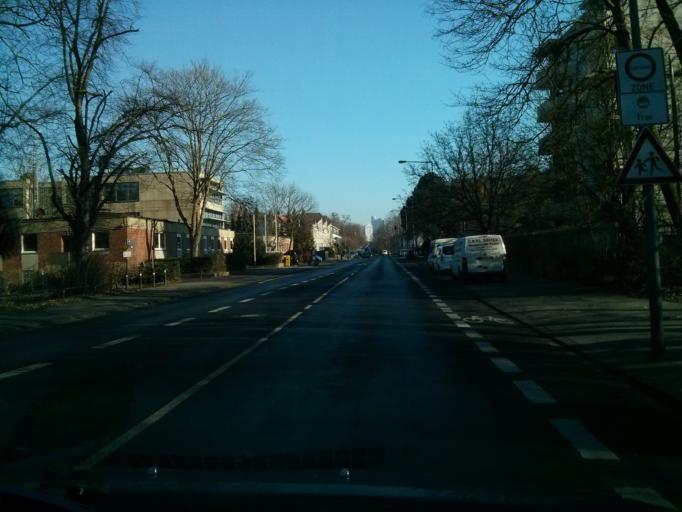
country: DE
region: North Rhine-Westphalia
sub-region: Regierungsbezirk Koln
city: Neustadt/Sued
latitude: 50.9068
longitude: 6.9126
